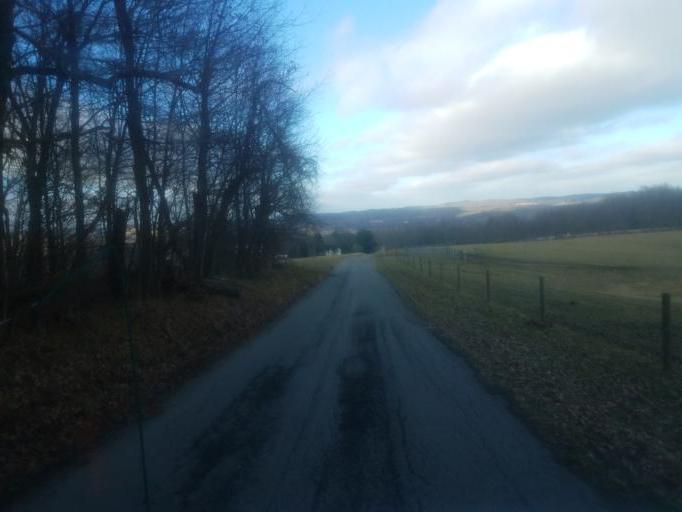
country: US
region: Ohio
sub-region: Ashland County
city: Loudonville
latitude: 40.6269
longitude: -82.3673
